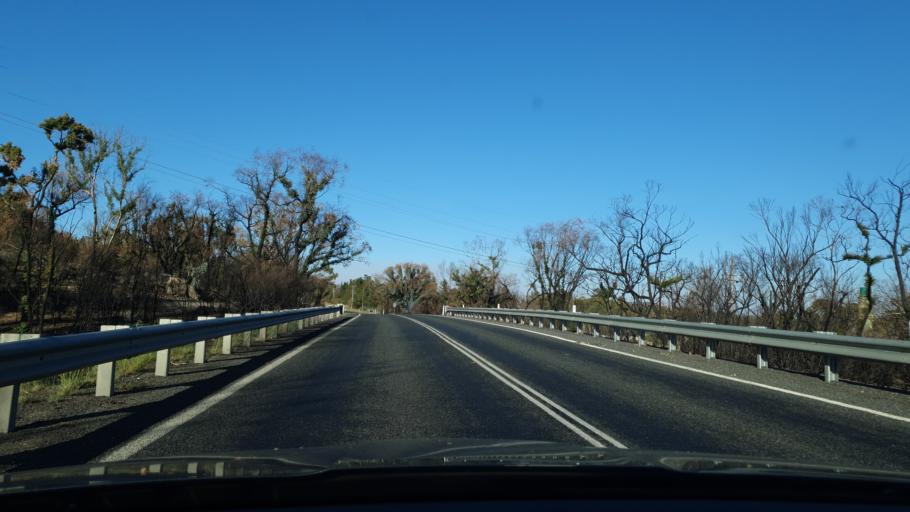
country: AU
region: Queensland
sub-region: Southern Downs
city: Stanthorpe
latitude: -28.6507
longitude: 151.9213
